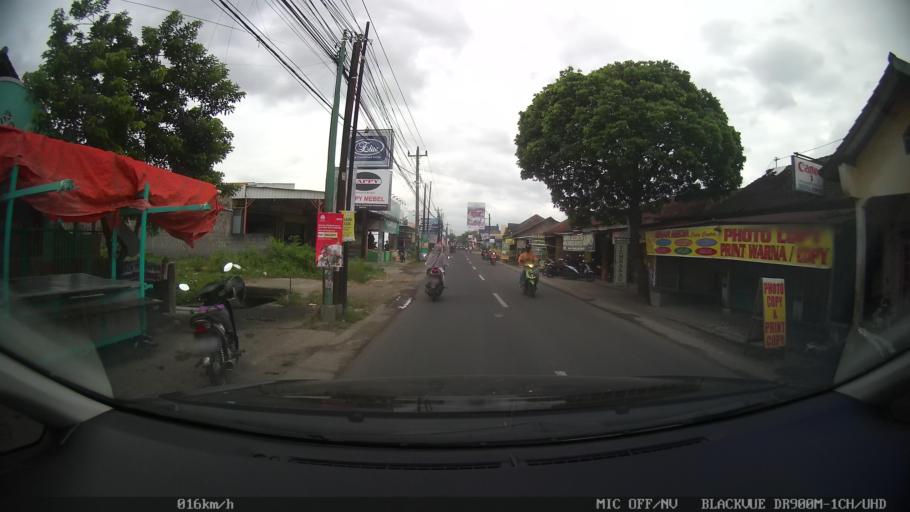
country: ID
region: Daerah Istimewa Yogyakarta
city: Sewon
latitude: -7.8423
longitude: 110.4112
